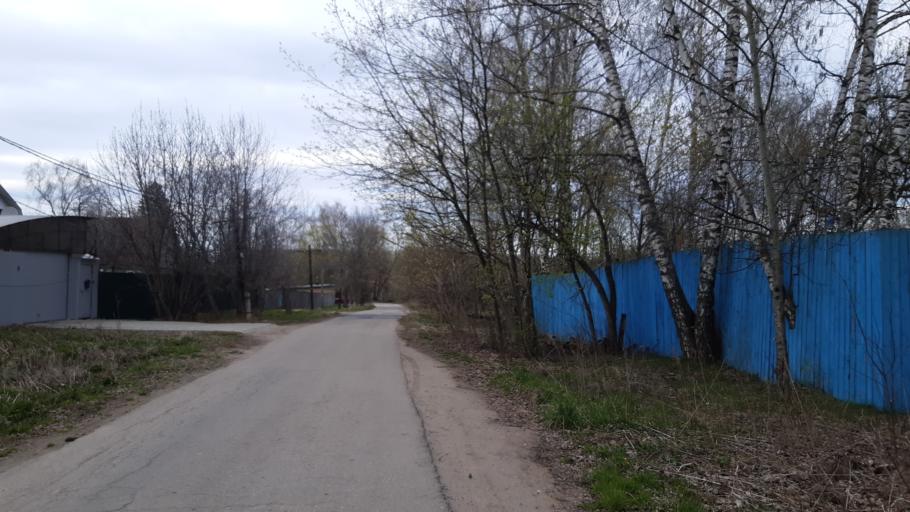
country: RU
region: Moscow
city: Severnyy
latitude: 55.9298
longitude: 37.5279
